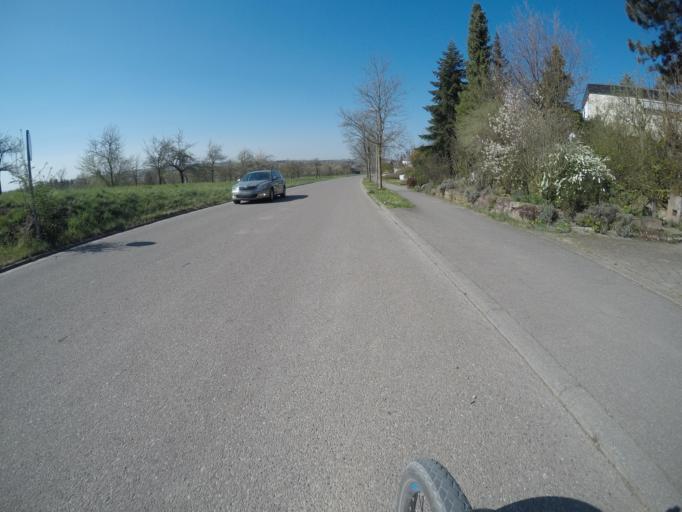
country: DE
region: Baden-Wuerttemberg
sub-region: Regierungsbezirk Stuttgart
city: Herrenberg
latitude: 48.5625
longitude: 8.9167
